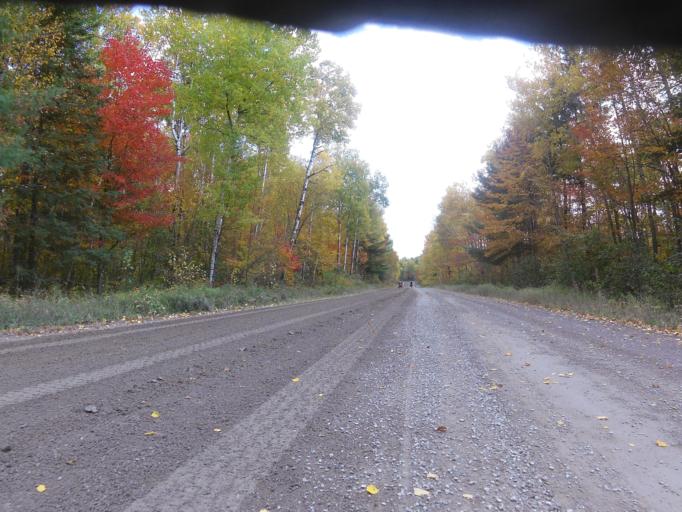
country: CA
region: Ontario
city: Petawawa
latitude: 45.8144
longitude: -77.3842
